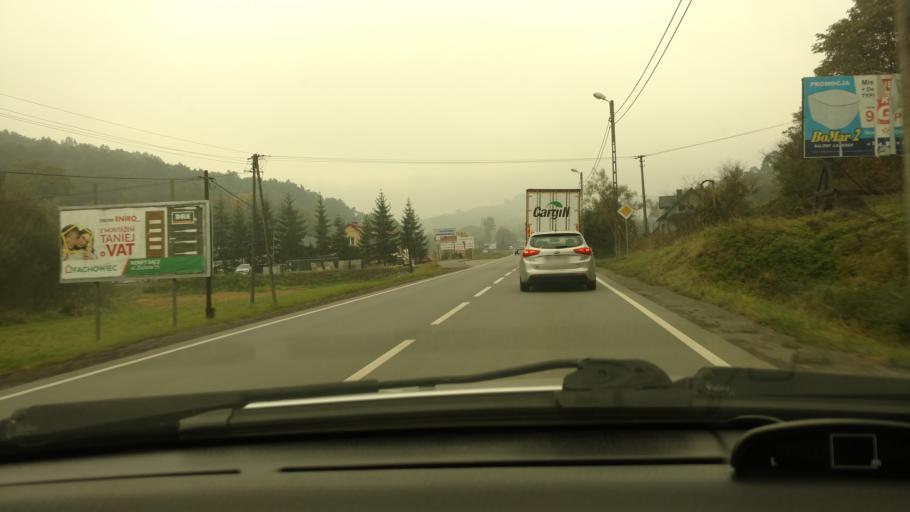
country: PL
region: Lesser Poland Voivodeship
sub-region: Powiat nowosadecki
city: Nawojowa
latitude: 49.6145
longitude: 20.7529
